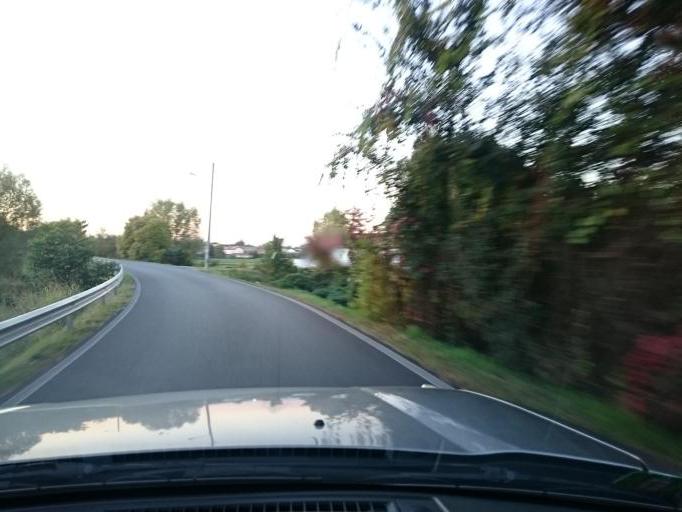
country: IT
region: Veneto
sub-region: Provincia di Padova
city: Mandriola-Sant'Agostino
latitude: 45.3876
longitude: 11.8506
